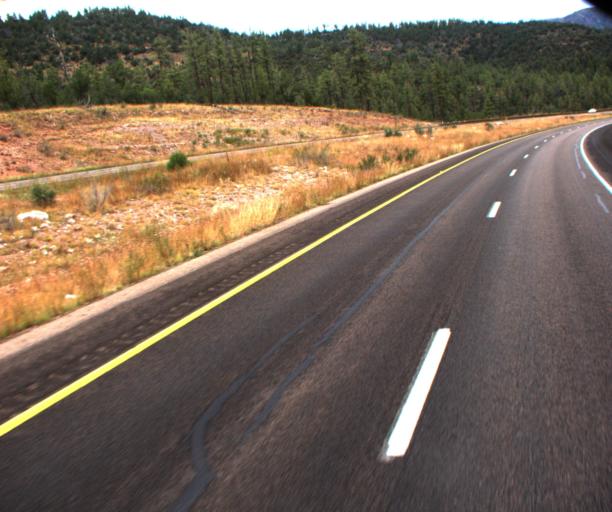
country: US
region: Arizona
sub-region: Gila County
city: Star Valley
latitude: 34.3205
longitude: -111.1140
